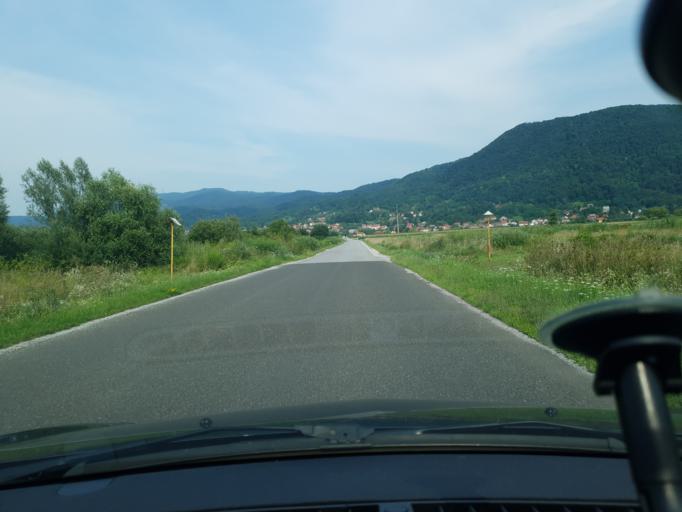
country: HR
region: Zagrebacka
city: Jablanovec
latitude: 45.8776
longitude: 15.8317
